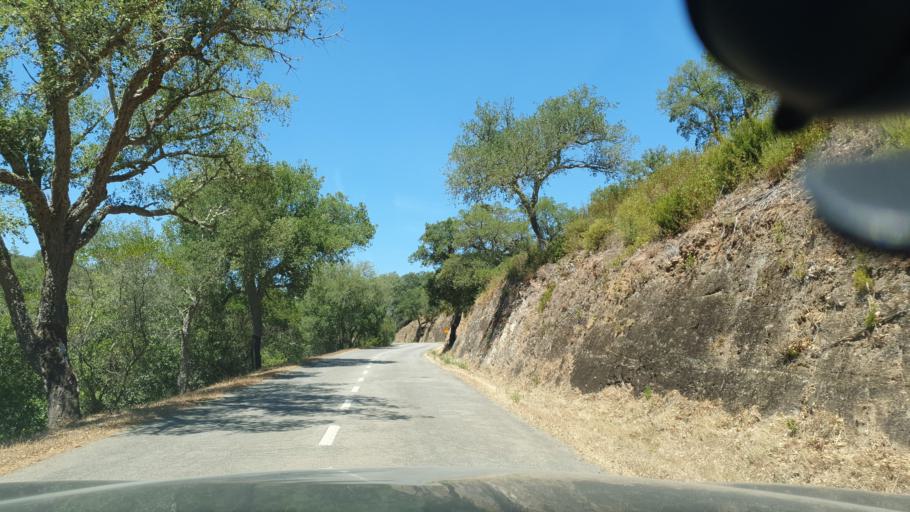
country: PT
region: Beja
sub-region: Odemira
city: Odemira
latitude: 37.5942
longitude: -8.4932
